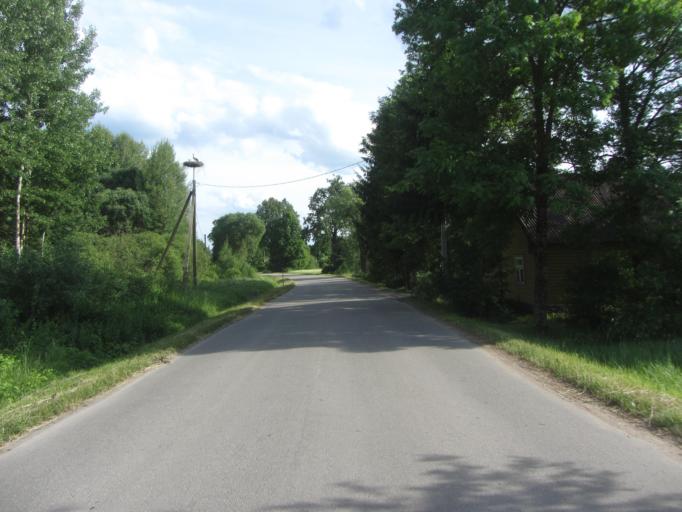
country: LT
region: Panevezys
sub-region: Birzai
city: Birzai
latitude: 56.2226
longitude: 24.7028
